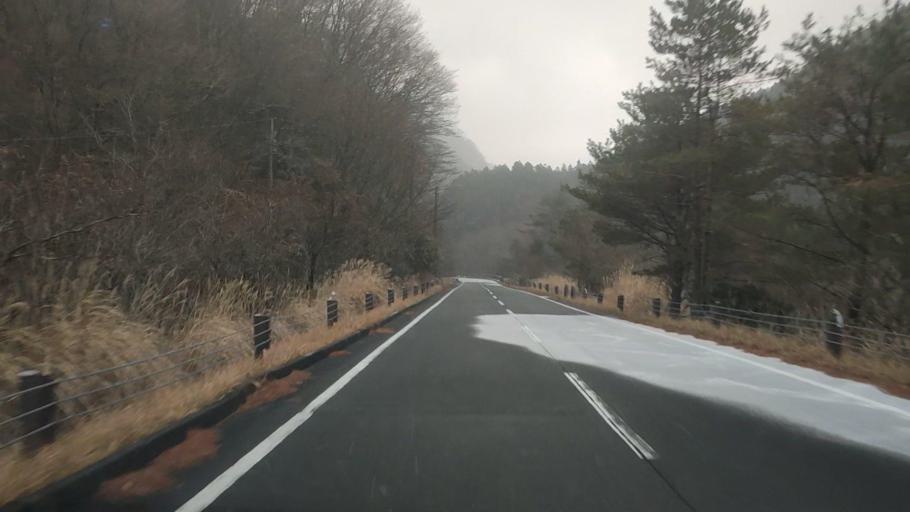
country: JP
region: Kumamoto
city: Matsubase
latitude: 32.5666
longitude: 130.9102
